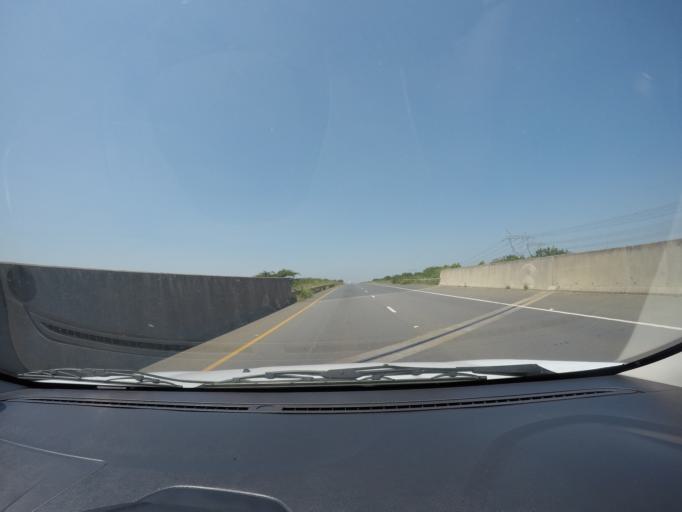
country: ZA
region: KwaZulu-Natal
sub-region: uThungulu District Municipality
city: Richards Bay
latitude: -28.7770
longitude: 32.0051
